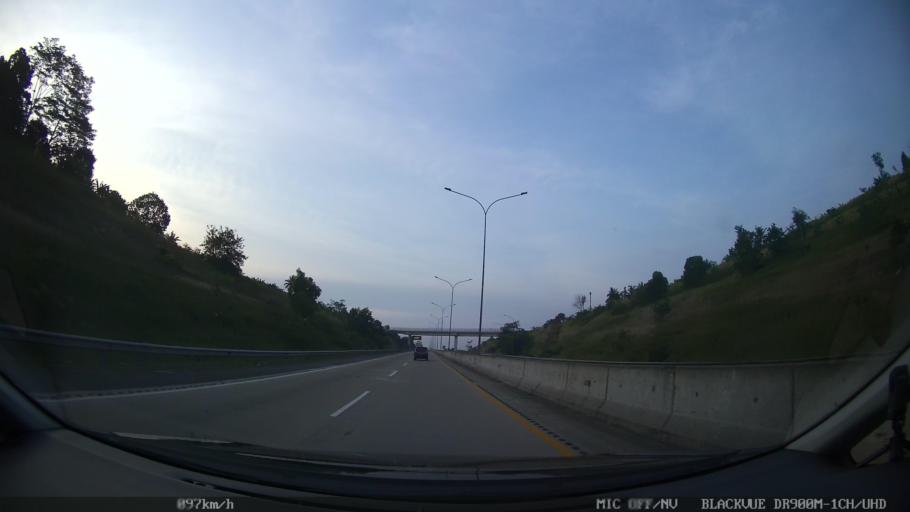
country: ID
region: Lampung
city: Penengahan
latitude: -5.8138
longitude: 105.7360
